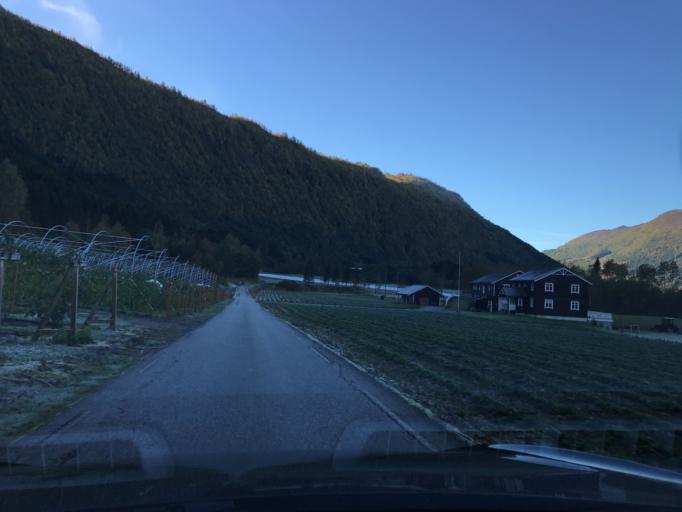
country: NO
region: More og Romsdal
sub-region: Norddal
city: Valldal
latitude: 62.3198
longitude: 7.3241
